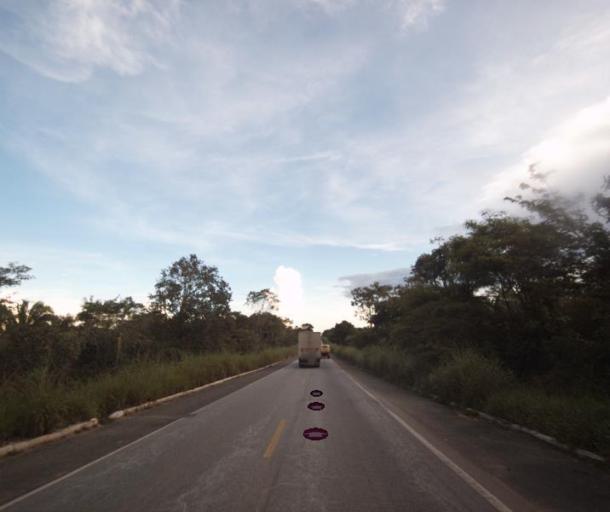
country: BR
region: Goias
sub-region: Uruacu
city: Uruacu
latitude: -14.2436
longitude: -49.1376
